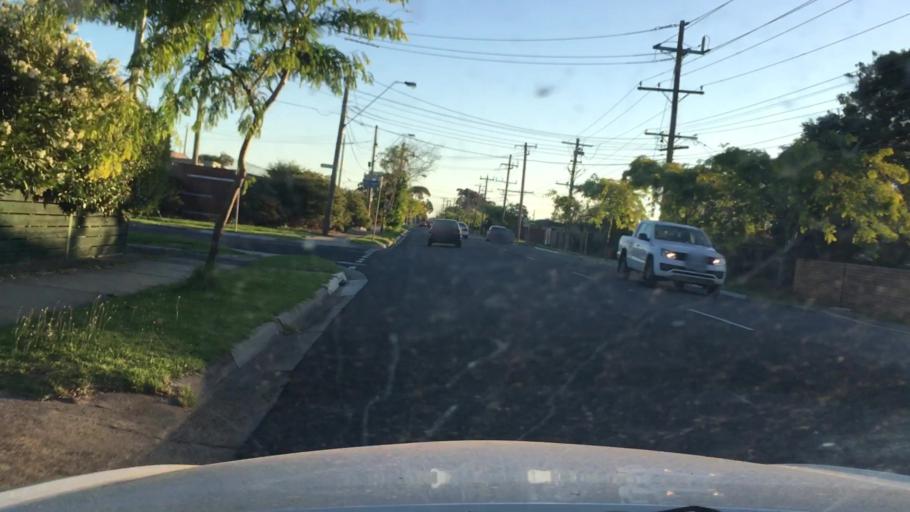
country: AU
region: Victoria
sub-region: Greater Dandenong
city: Noble Park
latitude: -37.9775
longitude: 145.1660
